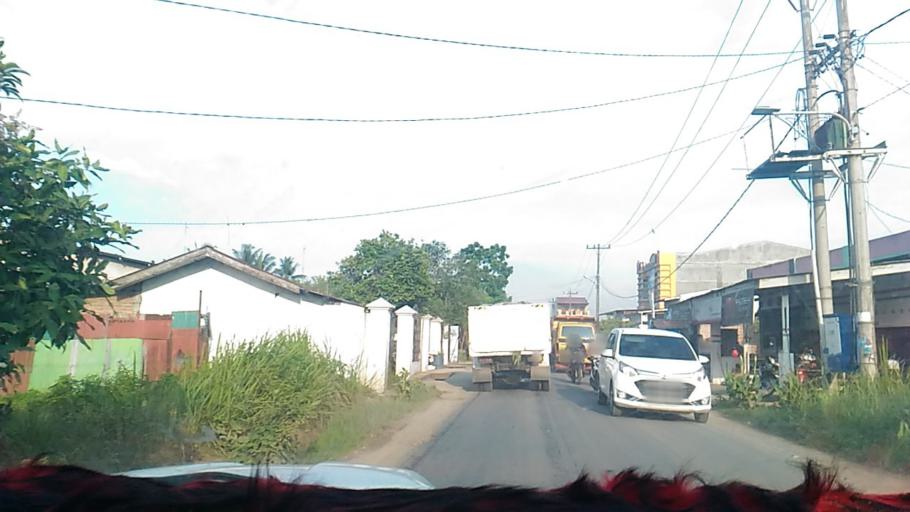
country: ID
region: North Sumatra
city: Labuhan Deli
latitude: 3.7073
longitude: 98.5992
